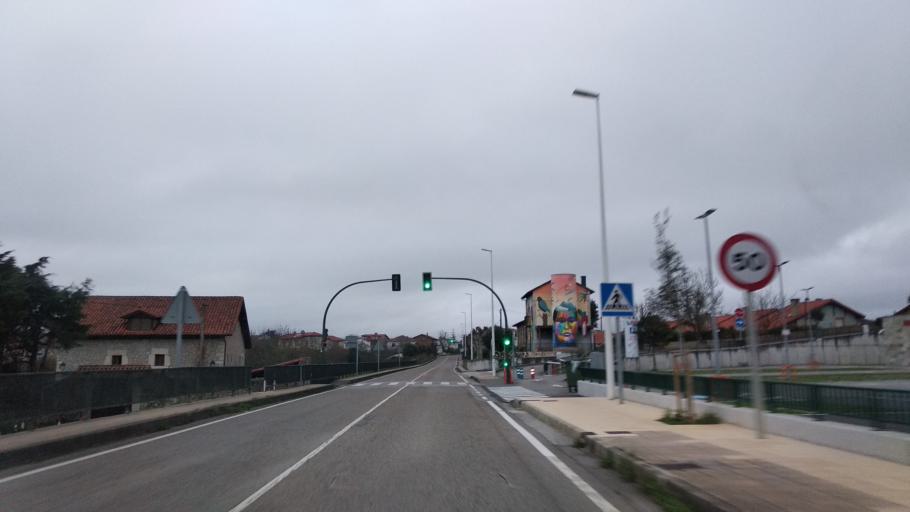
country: ES
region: Cantabria
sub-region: Provincia de Cantabria
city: Santander
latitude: 43.4510
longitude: -3.7339
